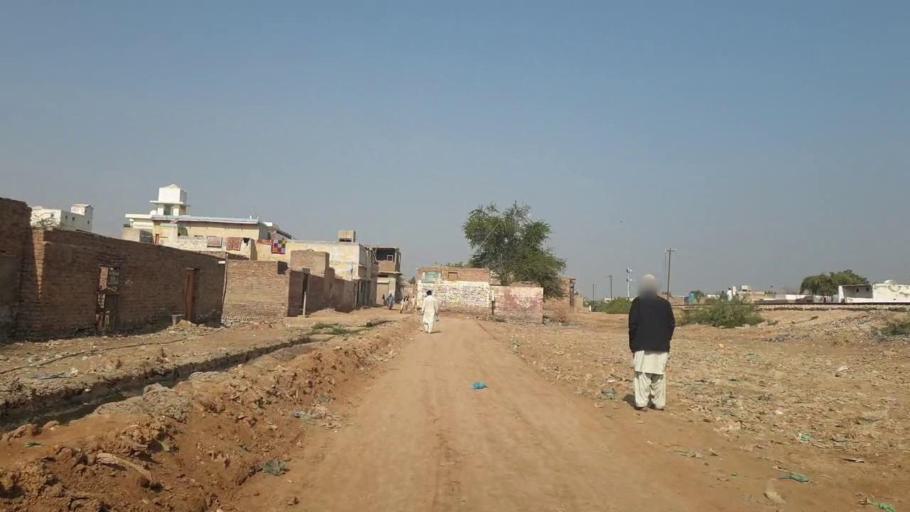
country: PK
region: Sindh
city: Jamshoro
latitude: 25.4339
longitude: 68.2805
